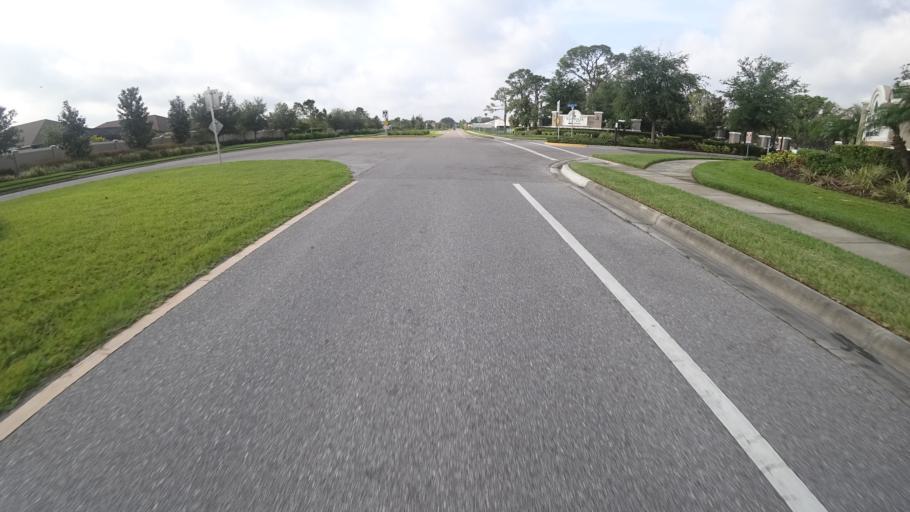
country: US
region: Florida
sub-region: Sarasota County
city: North Sarasota
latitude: 27.4181
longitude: -82.5133
